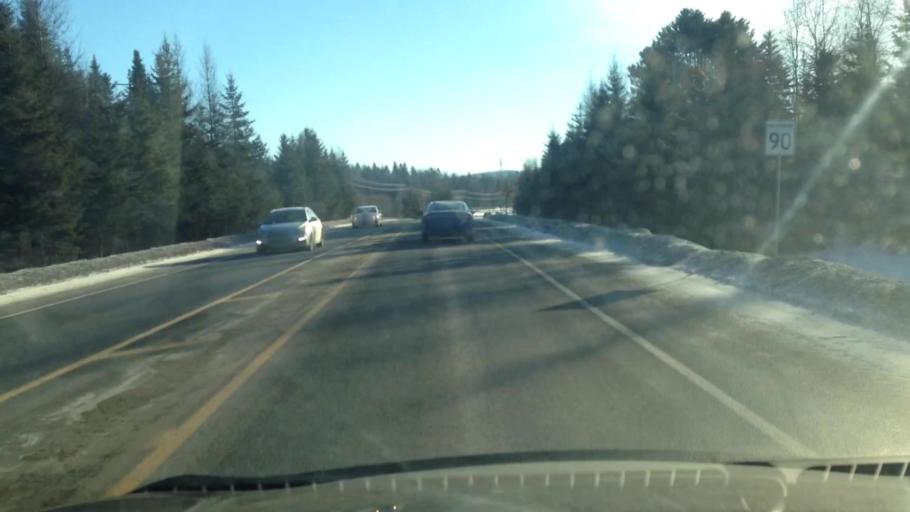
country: CA
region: Quebec
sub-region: Laurentides
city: Saint-Sauveur
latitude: 45.8947
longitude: -74.2002
